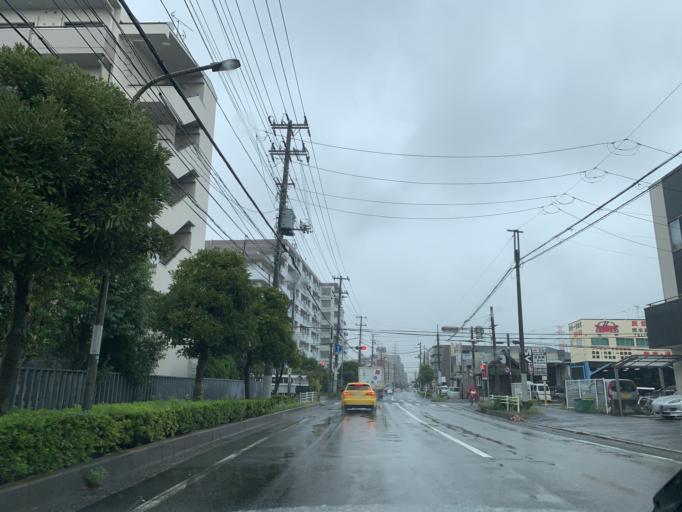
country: JP
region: Tokyo
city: Urayasu
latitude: 35.6660
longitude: 139.9039
